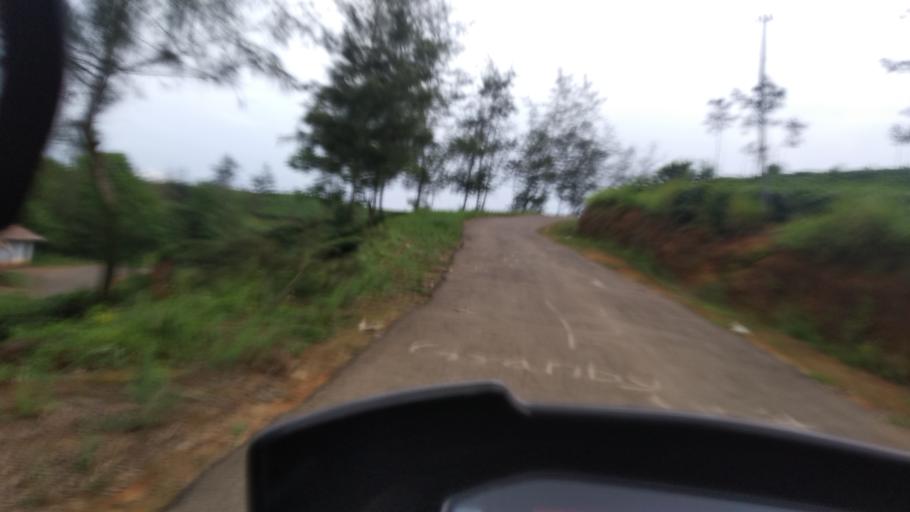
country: IN
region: Tamil Nadu
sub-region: Theni
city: Gudalur
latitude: 9.5442
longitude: 77.0394
